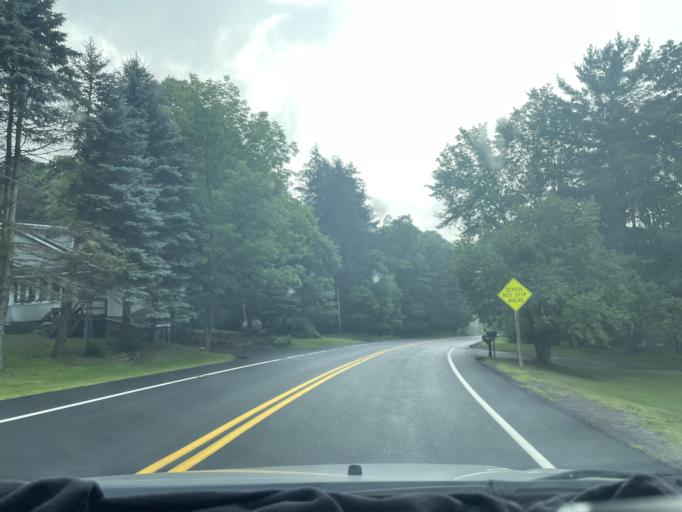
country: US
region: Maryland
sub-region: Garrett County
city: Mountain Lake Park
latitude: 39.3057
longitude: -79.4050
